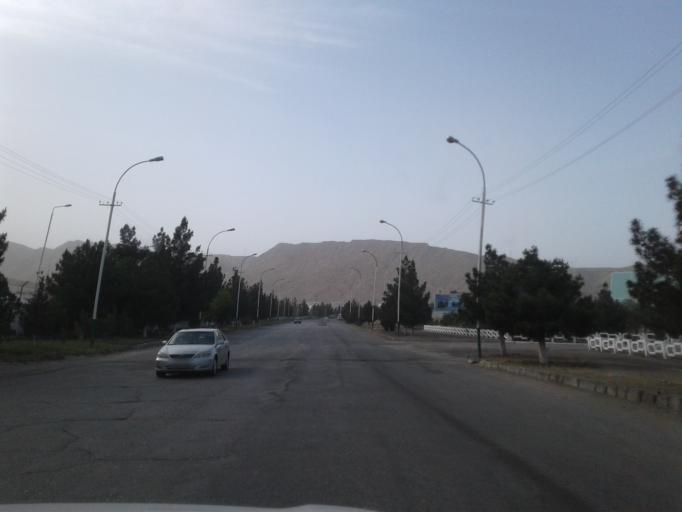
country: TM
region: Balkan
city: Turkmenbasy
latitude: 40.0268
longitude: 52.9676
